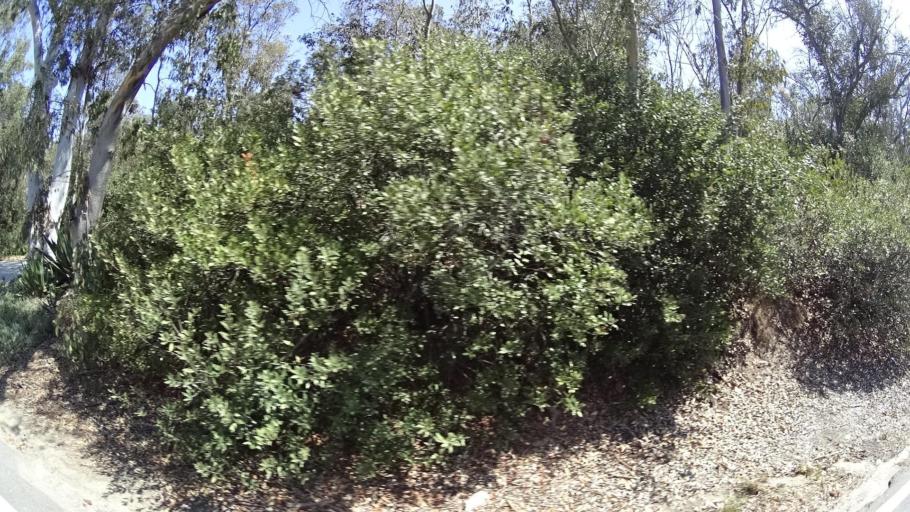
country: US
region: California
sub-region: San Diego County
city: Rancho Santa Fe
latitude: 33.0145
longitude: -117.2301
